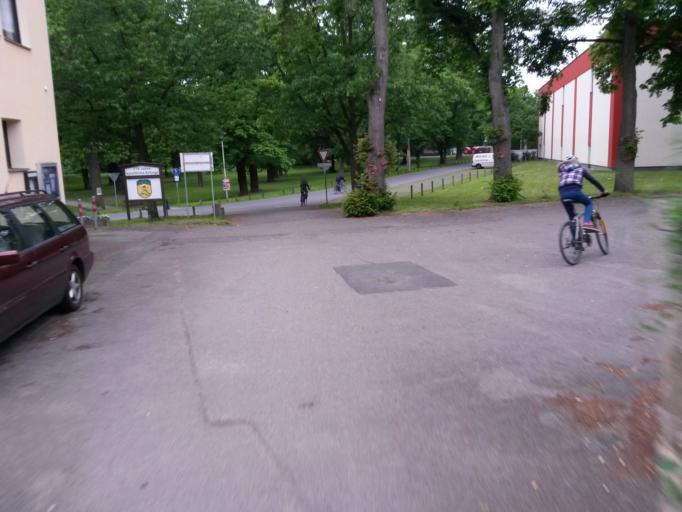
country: DE
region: Bavaria
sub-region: Regierungsbezirk Mittelfranken
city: Zirndorf
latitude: 49.4410
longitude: 10.9679
